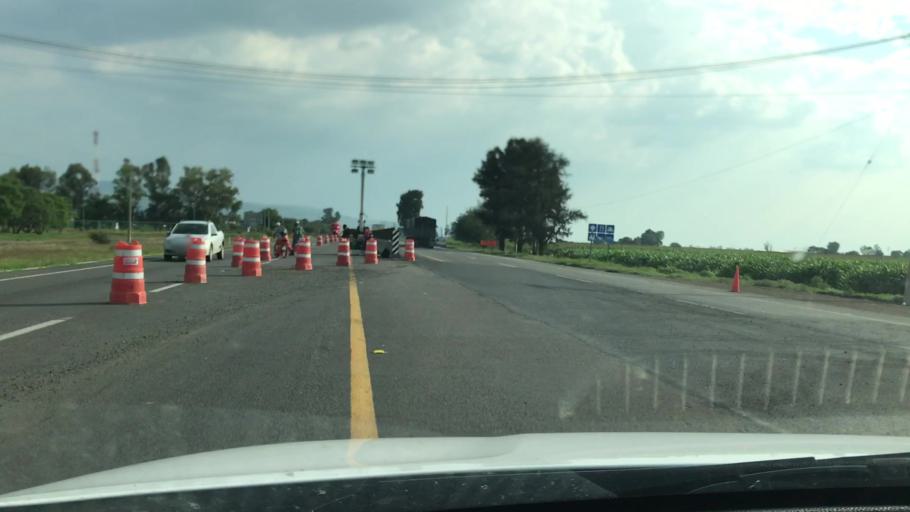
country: MX
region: Guanajuato
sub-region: Abasolo
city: San Bernardo Pena Blanca
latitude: 20.4997
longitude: -101.4800
